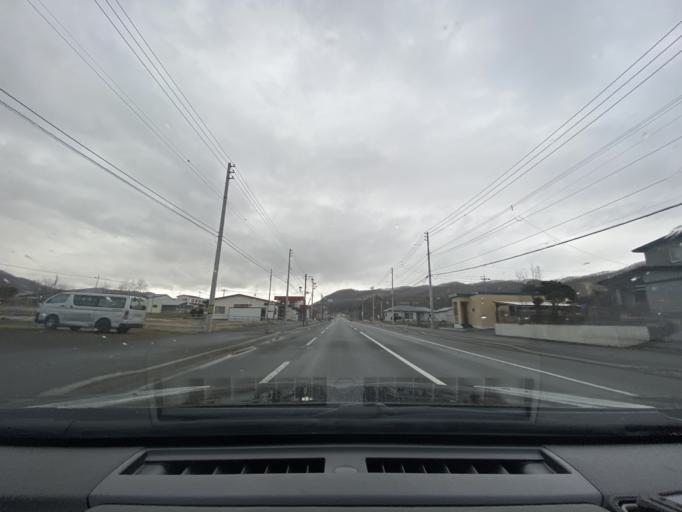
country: JP
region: Hokkaido
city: Otofuke
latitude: 43.2507
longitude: 143.5475
